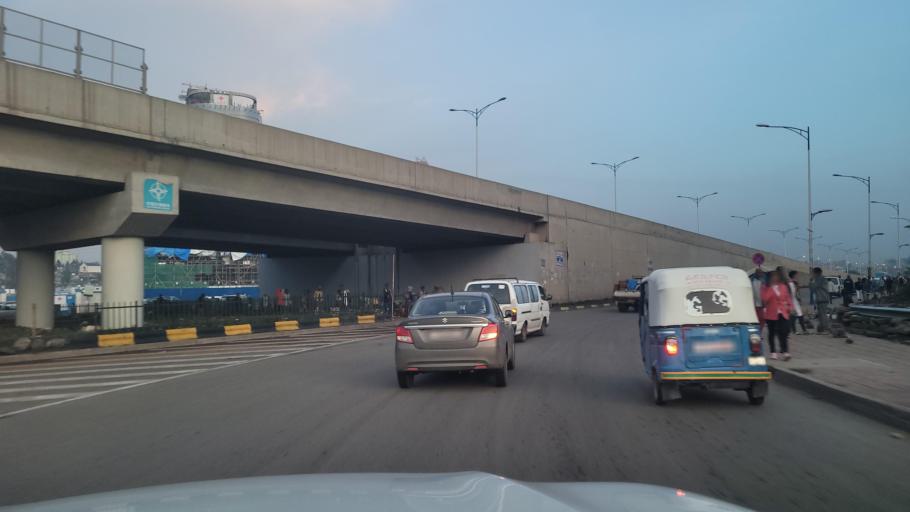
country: ET
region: Adis Abeba
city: Addis Ababa
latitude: 8.9364
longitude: 38.7342
